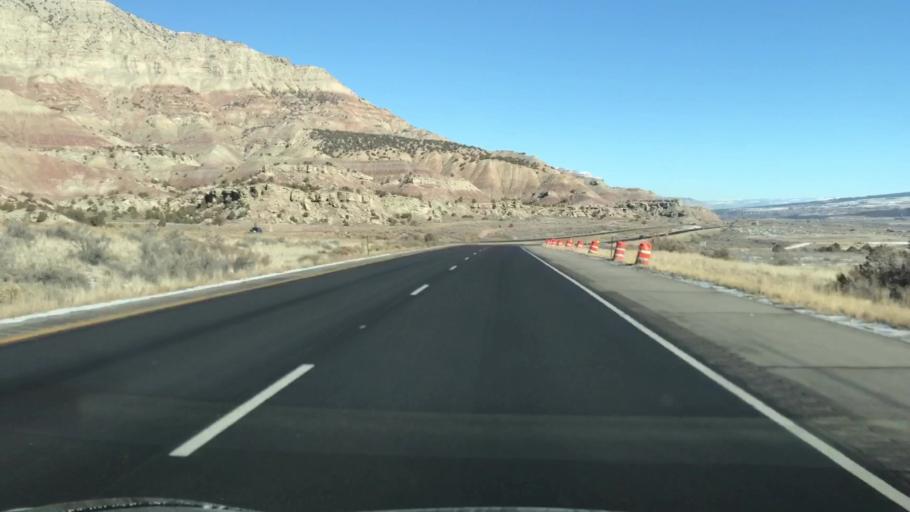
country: US
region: Colorado
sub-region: Garfield County
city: Parachute
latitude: 39.3938
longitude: -108.1266
